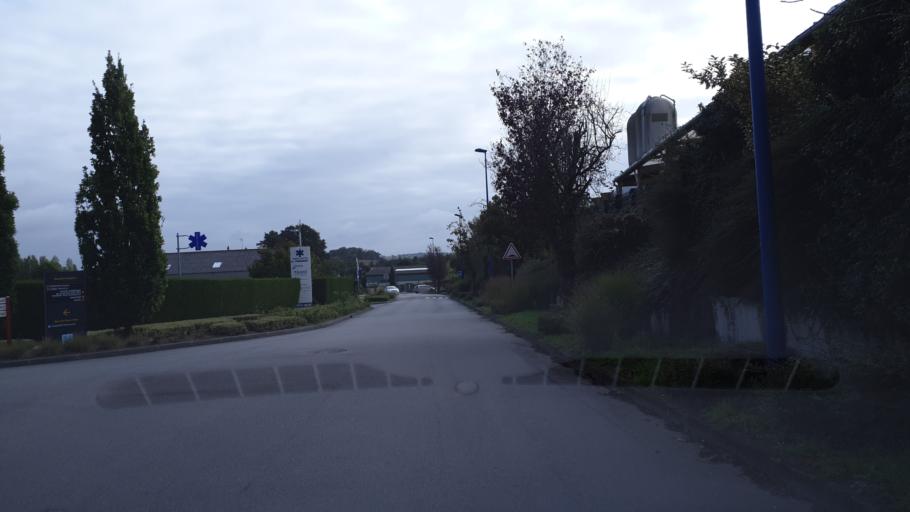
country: FR
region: Brittany
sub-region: Departement d'Ille-et-Vilaine
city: Janze
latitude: 47.9541
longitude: -1.4935
